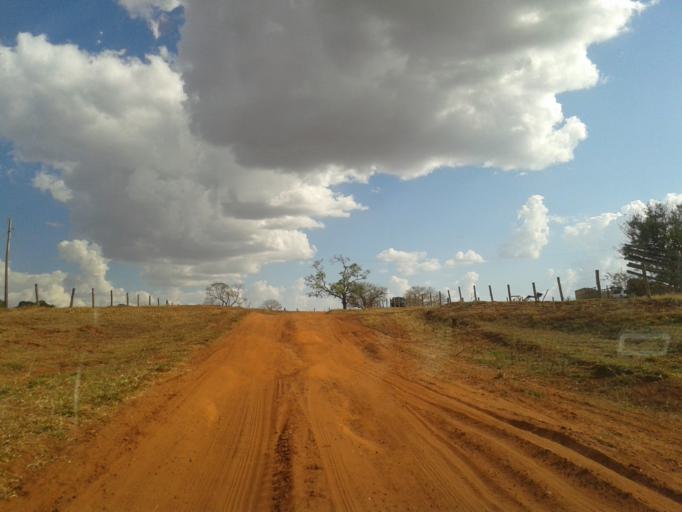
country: BR
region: Minas Gerais
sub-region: Santa Vitoria
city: Santa Vitoria
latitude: -19.2730
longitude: -49.9925
